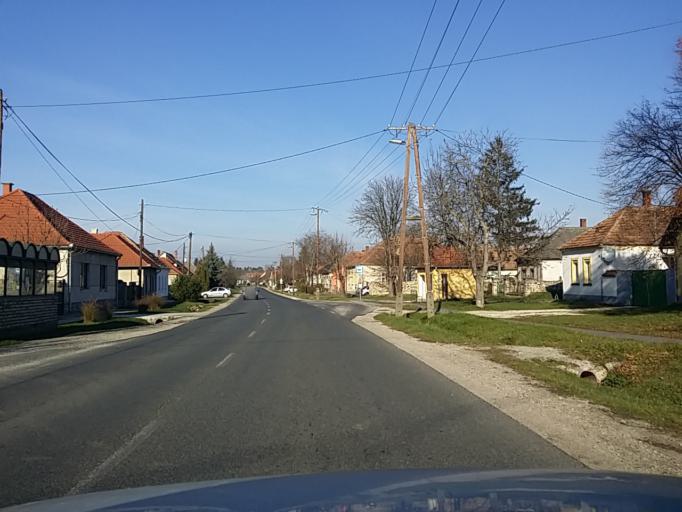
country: HU
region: Veszprem
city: Tapolca
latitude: 46.8682
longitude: 17.4805
